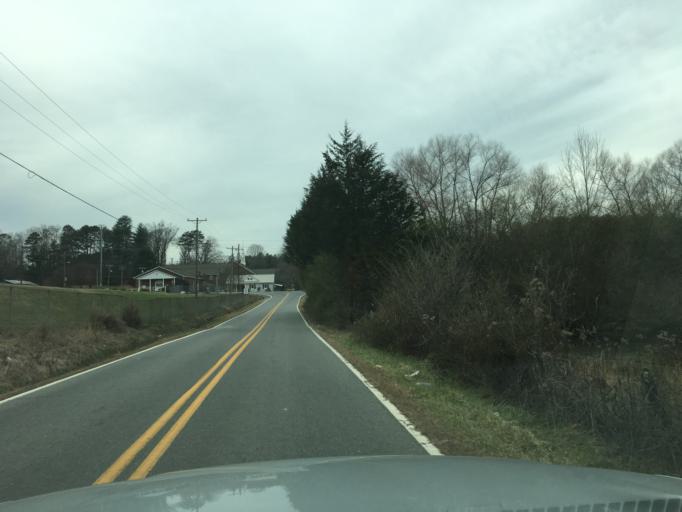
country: US
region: North Carolina
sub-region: McDowell County
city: West Marion
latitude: 35.6151
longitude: -81.9804
